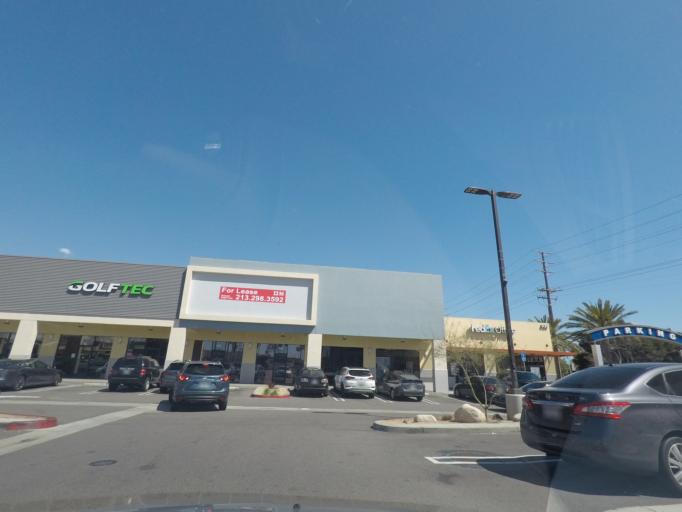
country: US
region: California
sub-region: Los Angeles County
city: El Segundo
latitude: 33.9241
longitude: -118.3953
